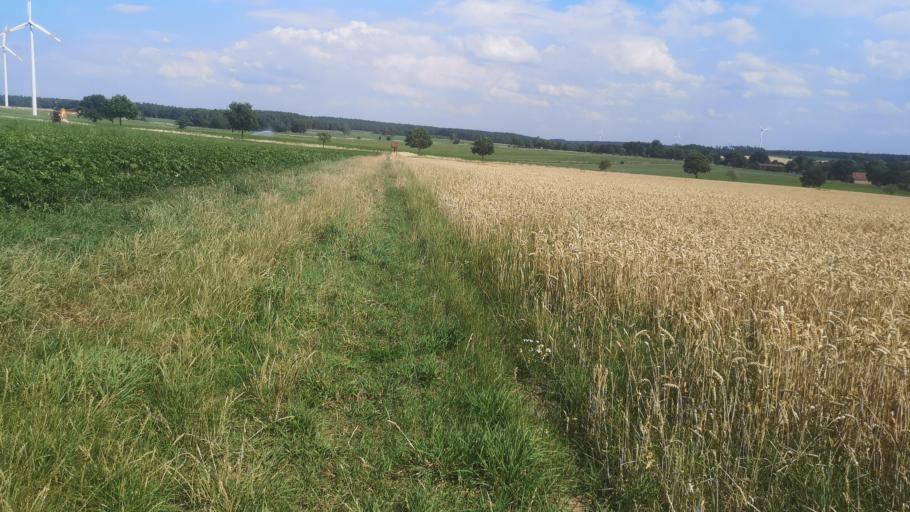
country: DE
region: Lower Saxony
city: Dahlem
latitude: 53.2220
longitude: 10.7512
